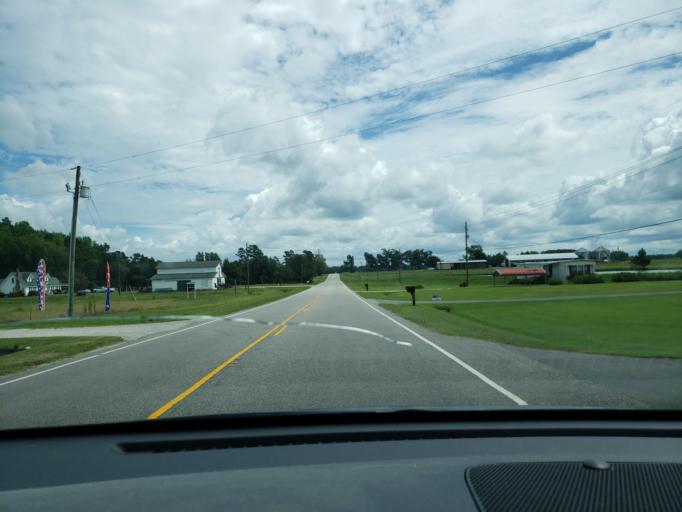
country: US
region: North Carolina
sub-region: Columbus County
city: Tabor City
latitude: 34.1873
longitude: -78.7863
